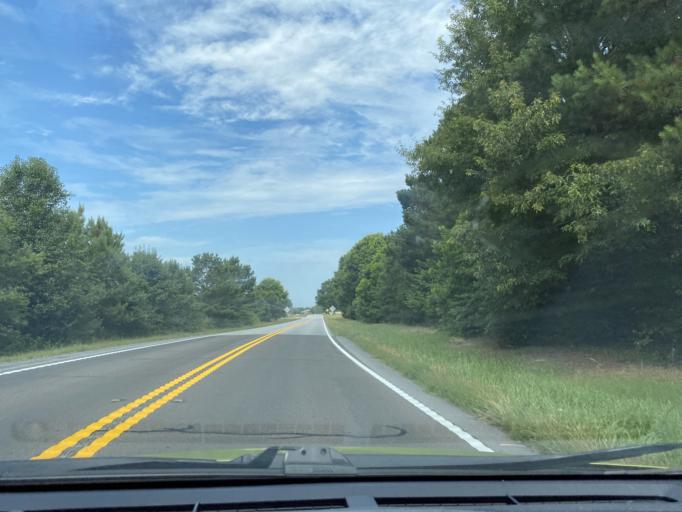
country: US
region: Georgia
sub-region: Coweta County
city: Senoia
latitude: 33.3037
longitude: -84.6569
